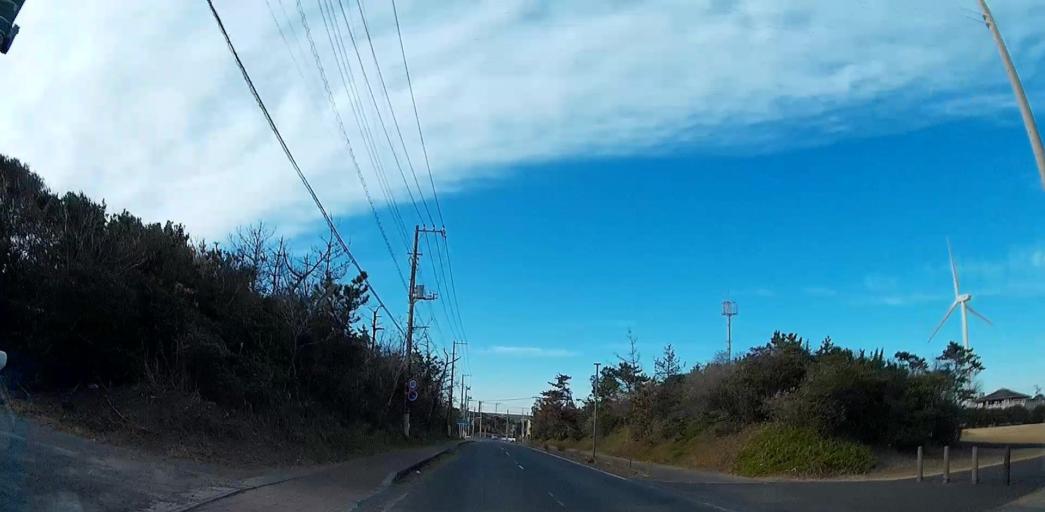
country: JP
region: Chiba
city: Hasaki
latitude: 35.7500
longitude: 140.8310
